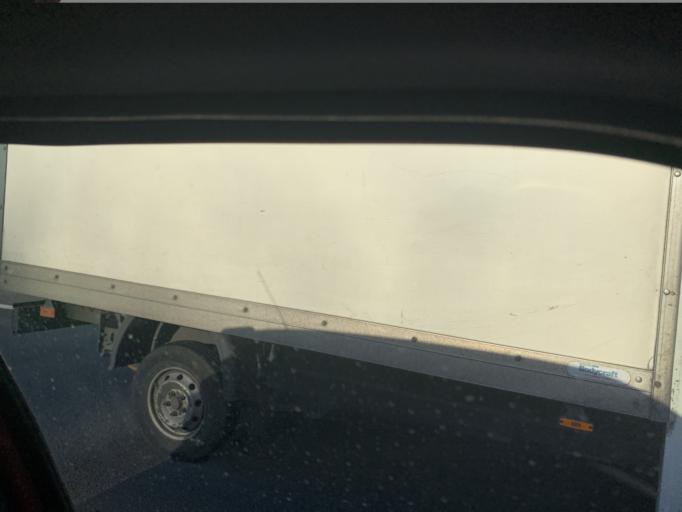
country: GB
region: England
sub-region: Surrey
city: Chertsey
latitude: 51.3892
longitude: -0.5270
